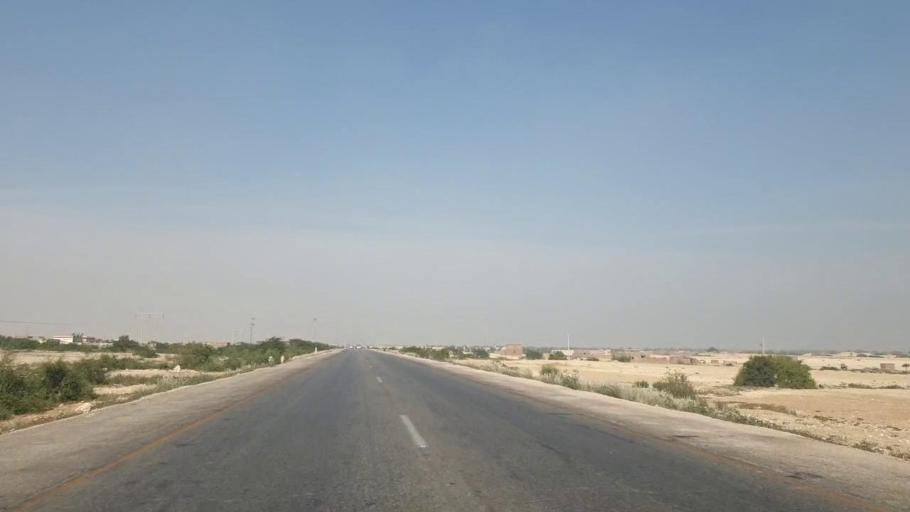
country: PK
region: Sindh
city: Hala
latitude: 25.8030
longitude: 68.2778
